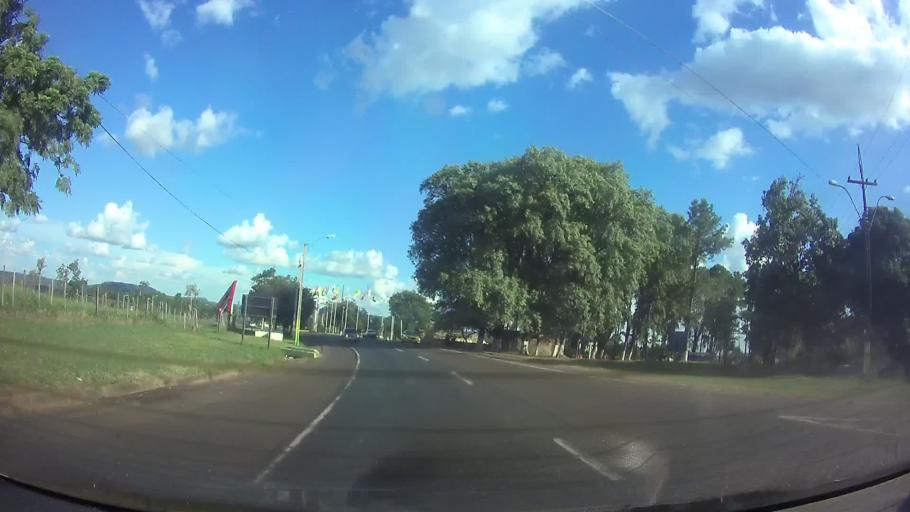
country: PY
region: Cordillera
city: Caacupe
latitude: -25.3867
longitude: -57.1965
